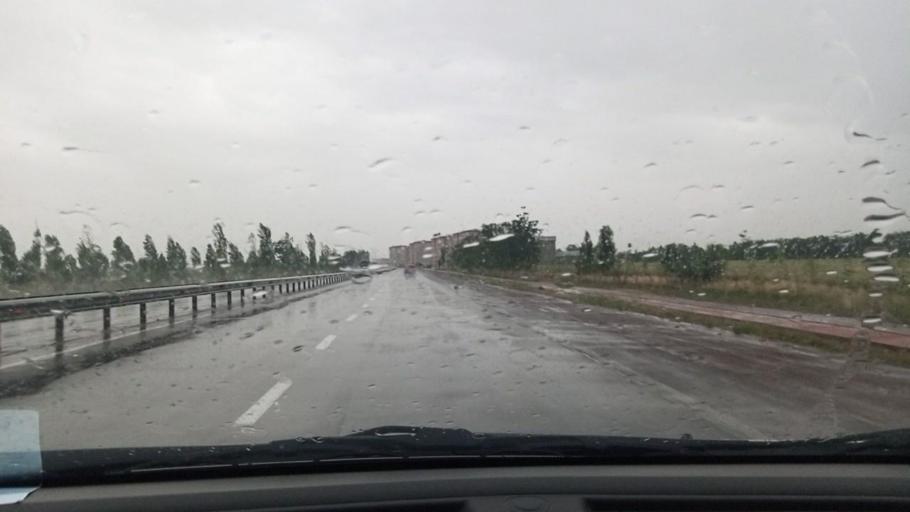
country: UZ
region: Toshkent
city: Ohangaron
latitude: 40.9171
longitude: 69.6037
